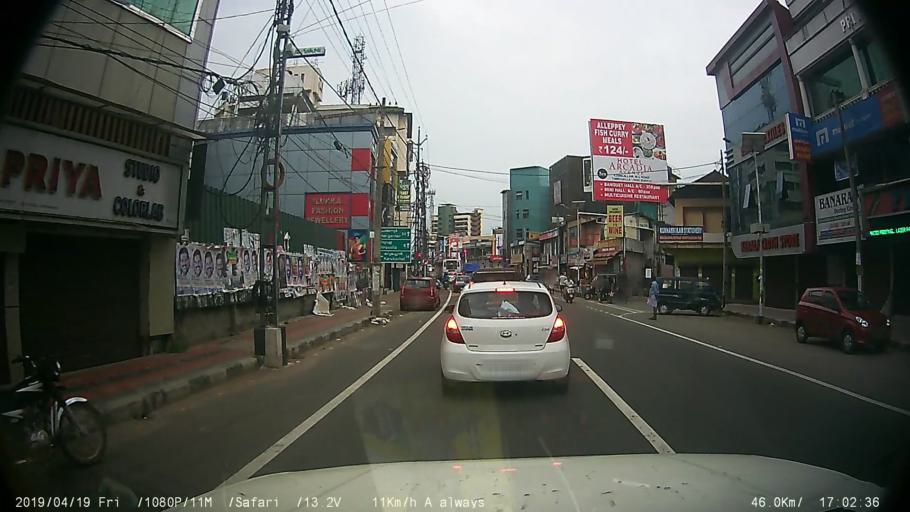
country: IN
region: Kerala
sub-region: Kottayam
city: Changanacheri
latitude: 9.4473
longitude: 76.5398
